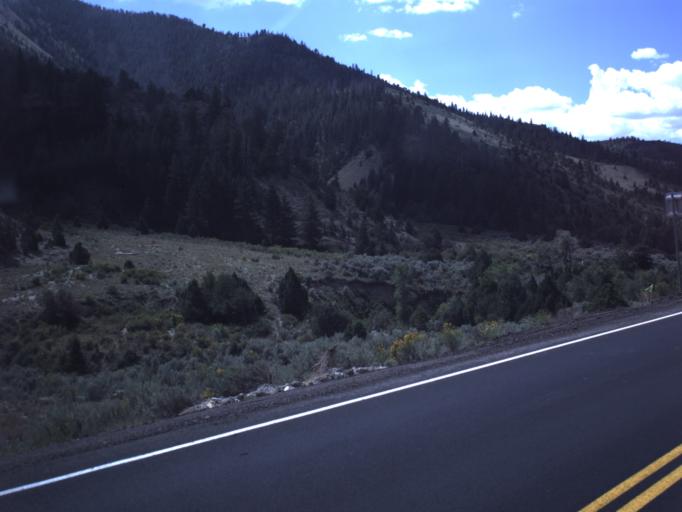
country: US
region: Utah
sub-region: Carbon County
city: Helper
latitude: 39.9460
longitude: -110.6594
